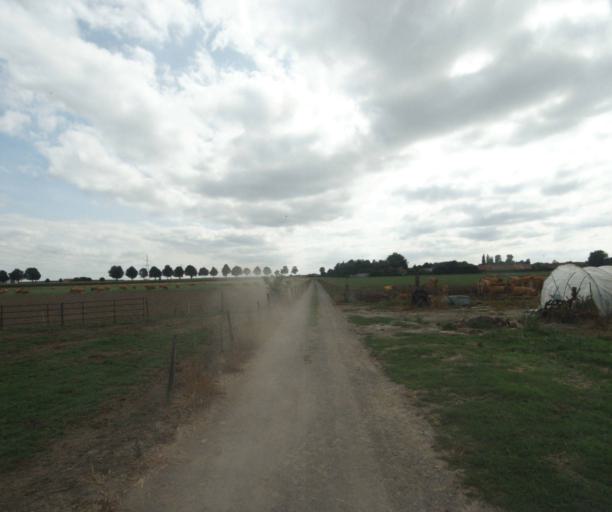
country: FR
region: Nord-Pas-de-Calais
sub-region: Departement du Nord
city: Chereng
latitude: 50.6136
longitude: 3.2203
